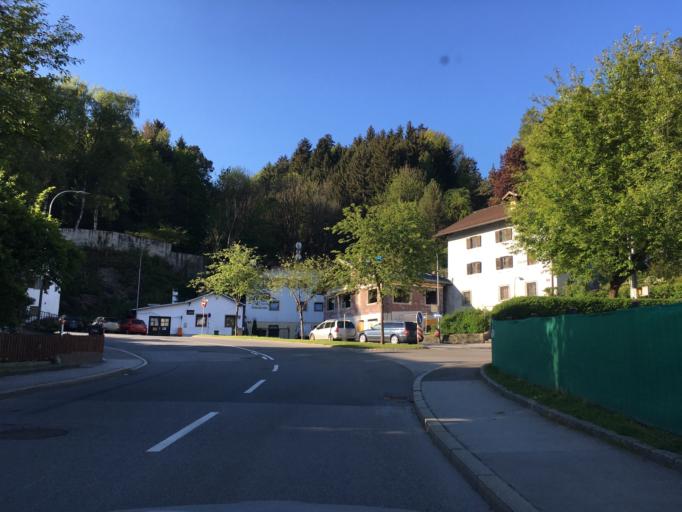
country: AT
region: Tyrol
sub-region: Politischer Bezirk Innsbruck Land
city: Ampass
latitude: 47.2592
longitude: 11.4351
